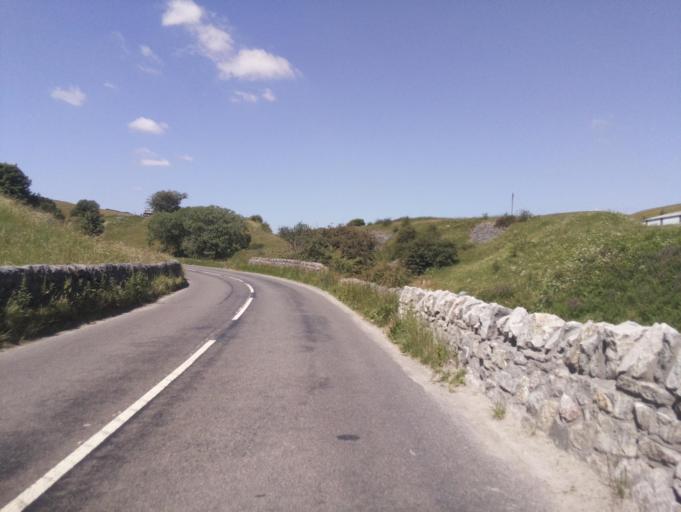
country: GB
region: England
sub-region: Derbyshire
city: Buxton
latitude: 53.2914
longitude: -1.8675
